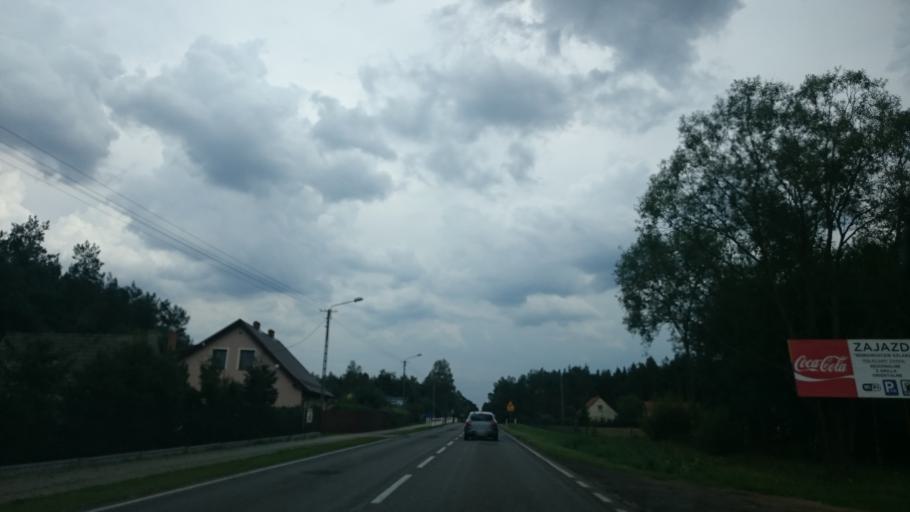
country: PL
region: Kujawsko-Pomorskie
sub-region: Powiat tucholski
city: Cekcyn
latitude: 53.5293
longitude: 17.9465
